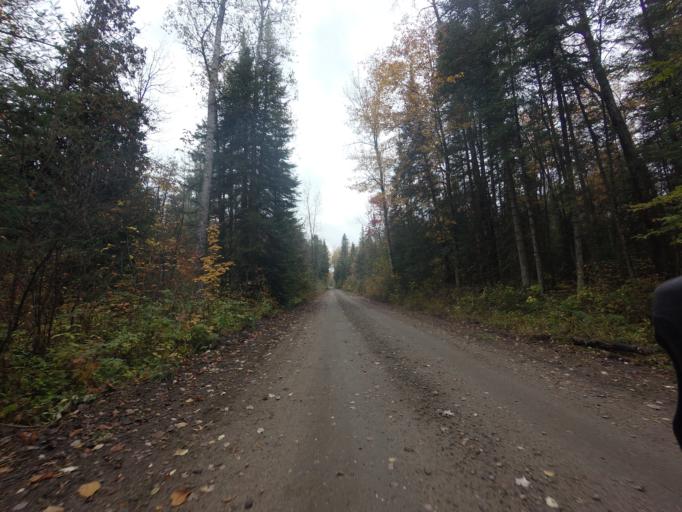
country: CA
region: Ontario
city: Renfrew
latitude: 45.1761
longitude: -76.6822
